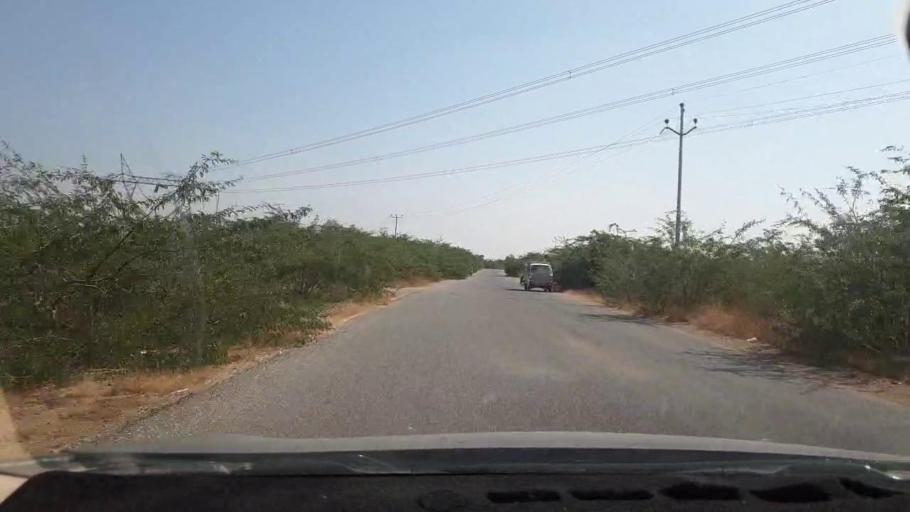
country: PK
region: Sindh
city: Malir Cantonment
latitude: 25.1434
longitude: 67.1929
